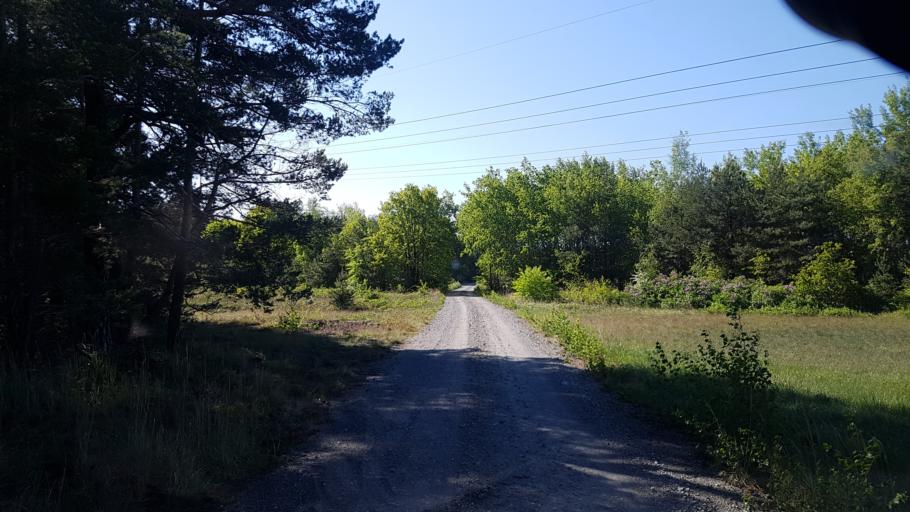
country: DE
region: Brandenburg
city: Grossraschen
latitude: 51.5903
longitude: 13.9611
